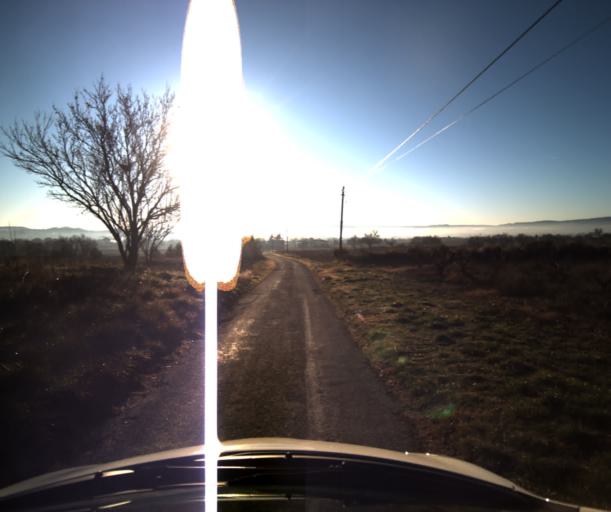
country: FR
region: Provence-Alpes-Cote d'Azur
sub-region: Departement du Vaucluse
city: Pertuis
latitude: 43.7065
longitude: 5.4875
